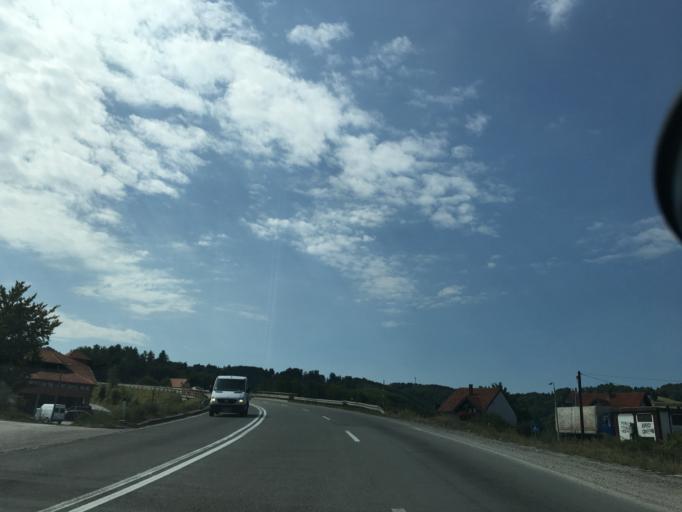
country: RS
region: Central Serbia
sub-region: Zlatiborski Okrug
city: Cajetina
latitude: 43.7508
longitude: 19.7098
